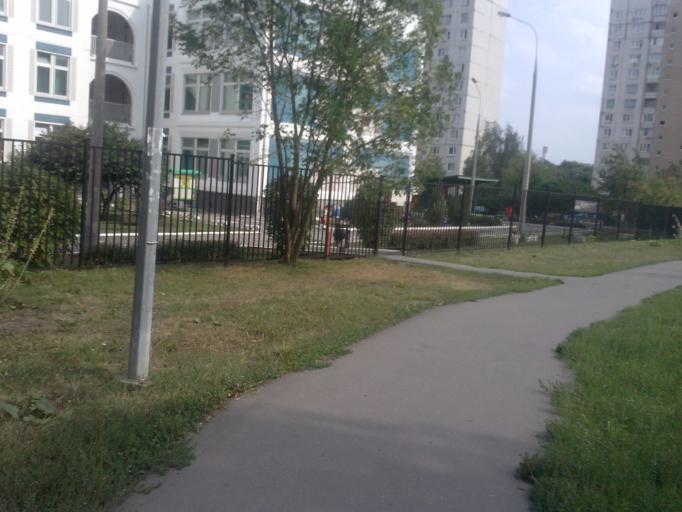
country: RU
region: Moskovskaya
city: Bol'shaya Setun'
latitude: 55.7160
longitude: 37.4129
